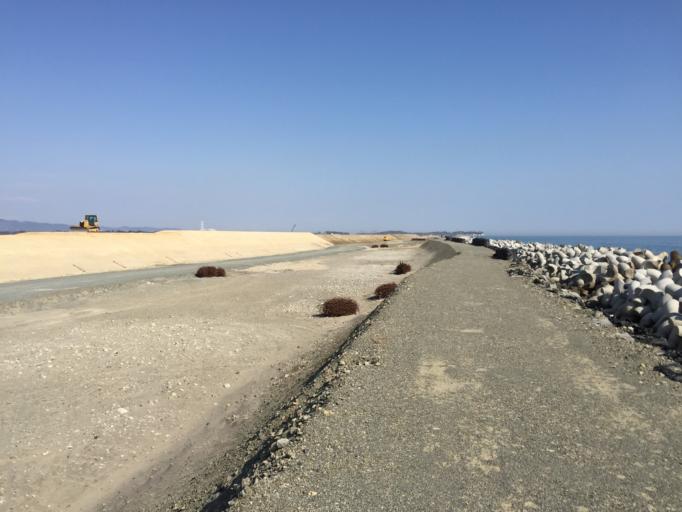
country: JP
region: Miyagi
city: Marumori
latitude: 37.7783
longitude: 140.9879
